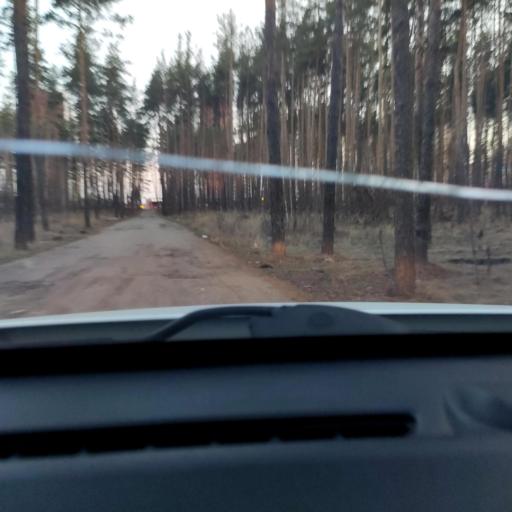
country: RU
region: Voronezj
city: Somovo
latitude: 51.7441
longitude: 39.3168
